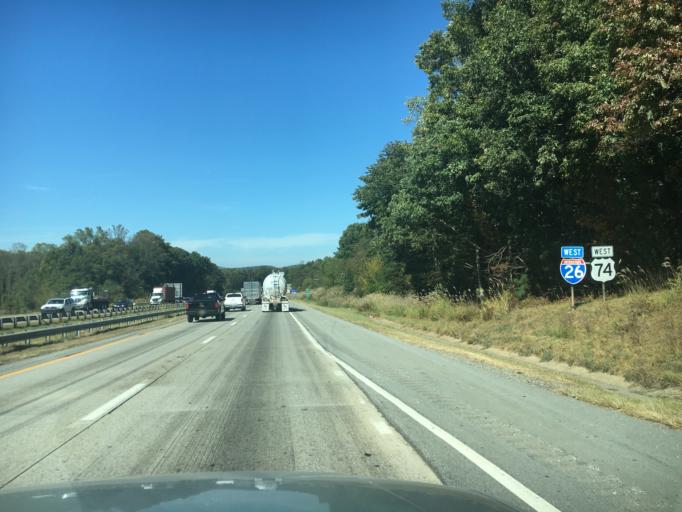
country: US
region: North Carolina
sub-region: Buncombe County
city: Royal Pines
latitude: 35.4457
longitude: -82.5390
